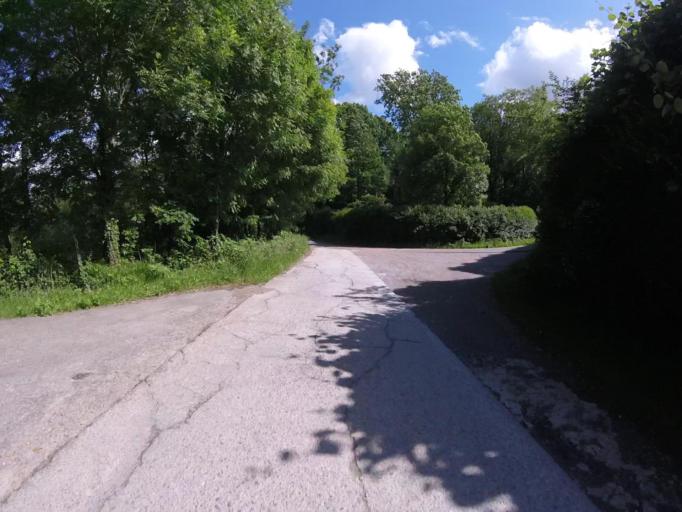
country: ES
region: Basque Country
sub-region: Provincia de Guipuzcoa
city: Errenteria
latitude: 43.2930
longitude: -1.9119
